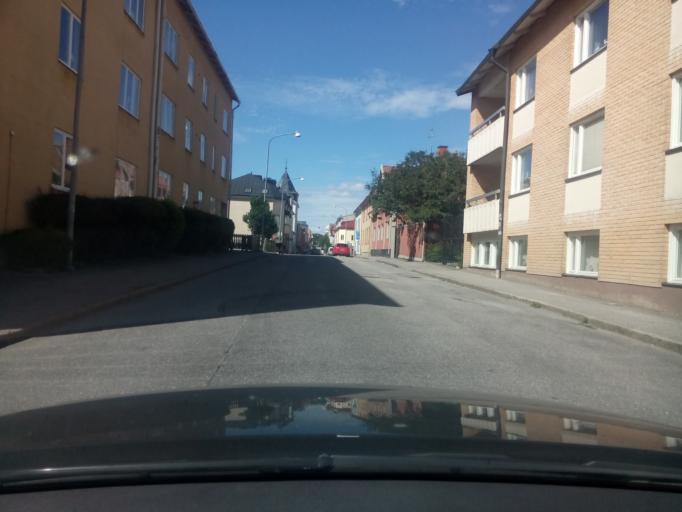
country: SE
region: Soedermanland
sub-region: Nykopings Kommun
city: Nykoping
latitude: 58.7501
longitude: 17.0072
